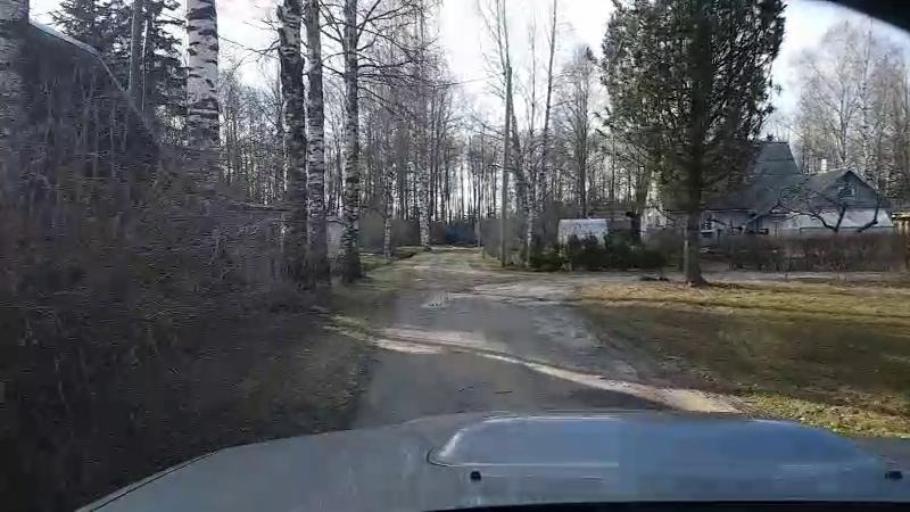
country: EE
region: Jaervamaa
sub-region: Paide linn
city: Paide
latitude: 58.8885
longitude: 25.5298
